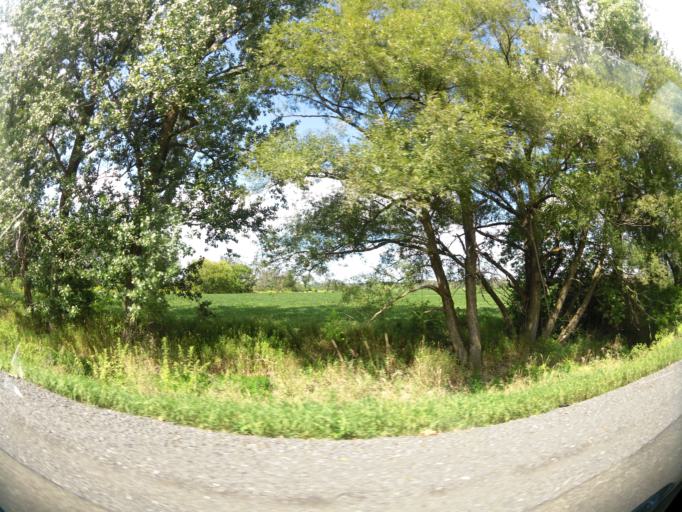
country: CA
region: Ontario
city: Ottawa
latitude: 45.4234
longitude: -75.5321
